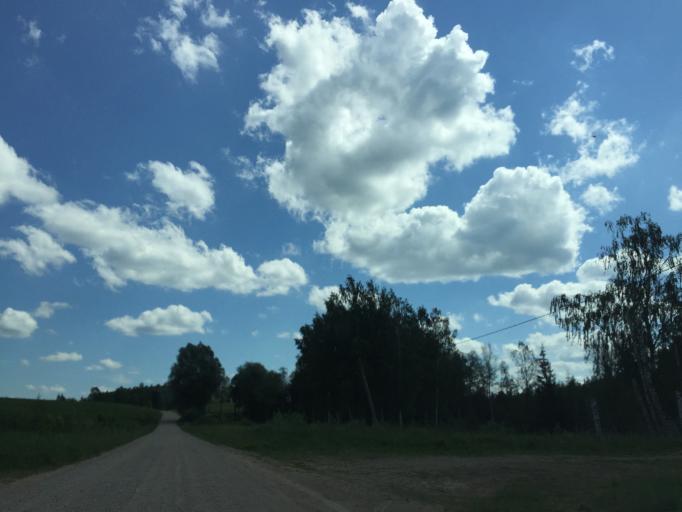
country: LV
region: Priekuli
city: Priekuli
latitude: 57.2561
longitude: 25.4291
